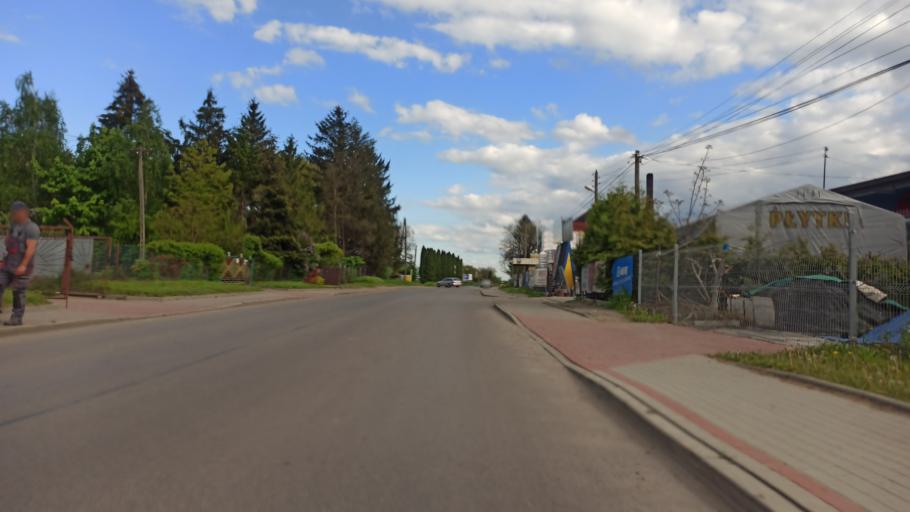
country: PL
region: Subcarpathian Voivodeship
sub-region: Powiat jaroslawski
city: Radymno
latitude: 49.9406
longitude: 22.8317
